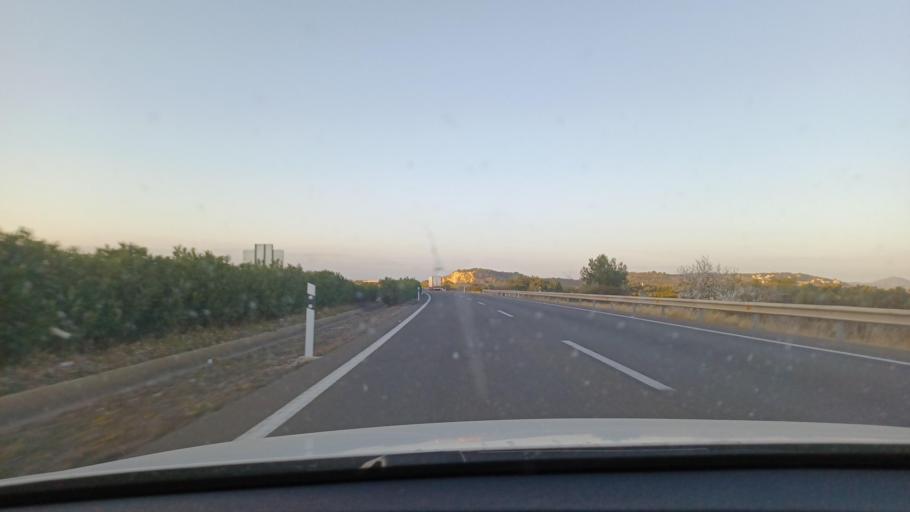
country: ES
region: Valencia
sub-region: Provincia de Castello
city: Vinaros
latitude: 40.4783
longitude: 0.4190
